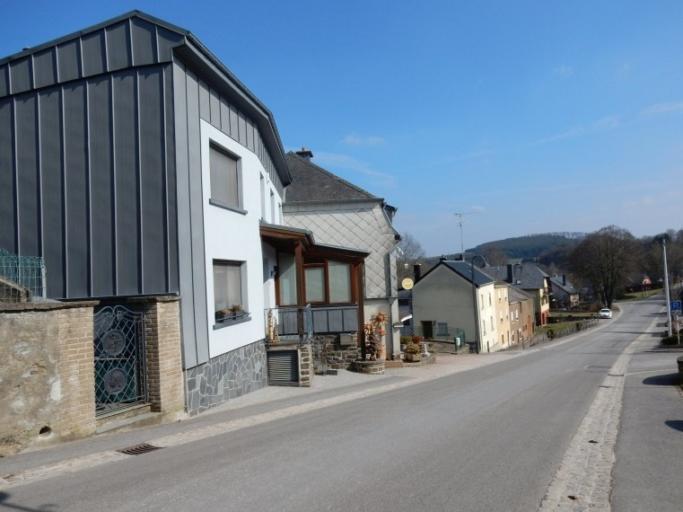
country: LU
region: Diekirch
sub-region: Canton de Wiltz
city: Winseler
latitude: 49.9671
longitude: 5.8893
